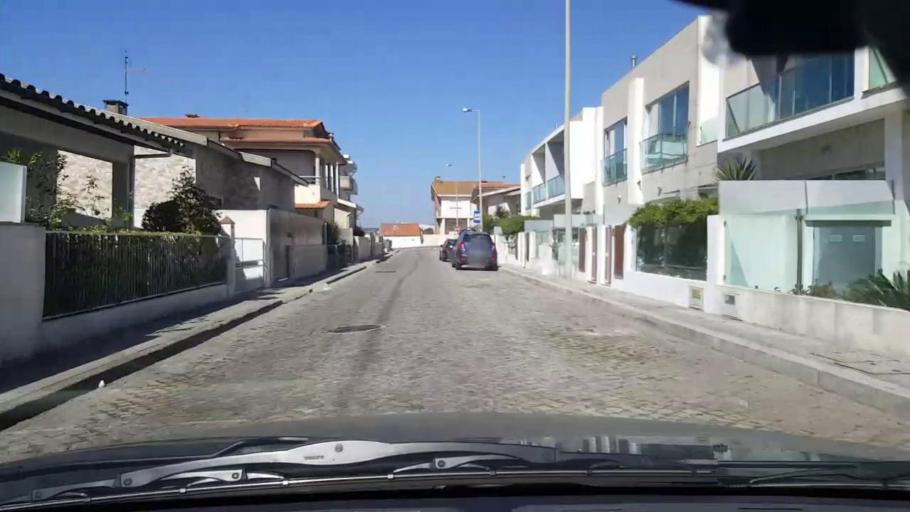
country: PT
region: Porto
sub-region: Vila do Conde
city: Arvore
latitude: 41.3094
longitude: -8.7353
